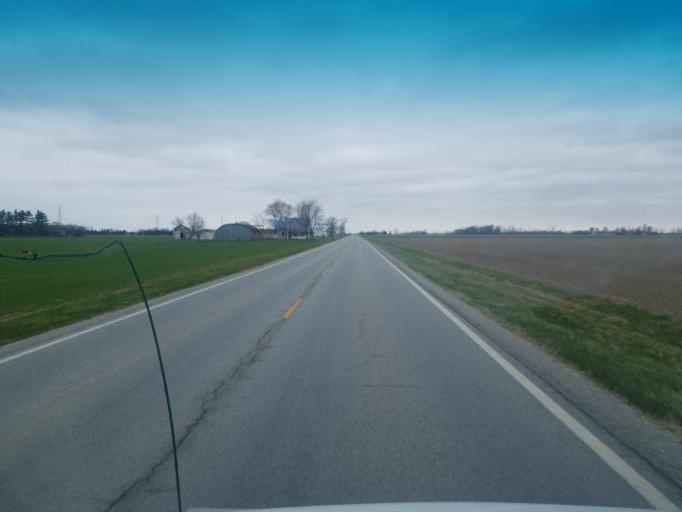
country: US
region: Ohio
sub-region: Allen County
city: Delphos
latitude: 40.9321
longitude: -84.4235
